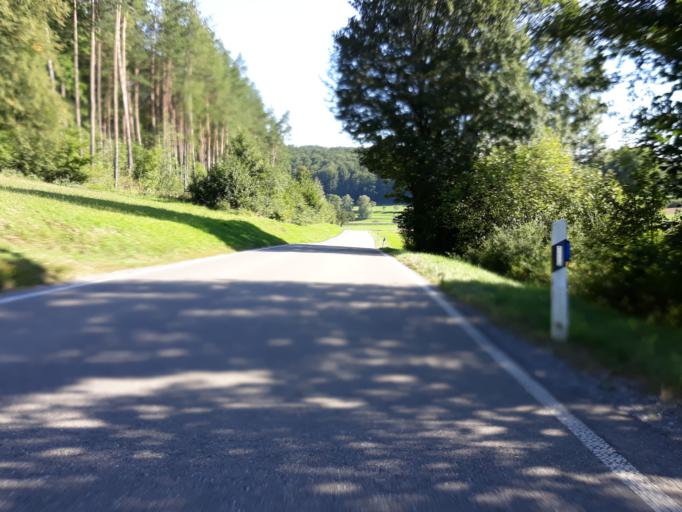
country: DE
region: Baden-Wuerttemberg
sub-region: Karlsruhe Region
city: Gechingen
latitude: 48.7042
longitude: 8.8390
